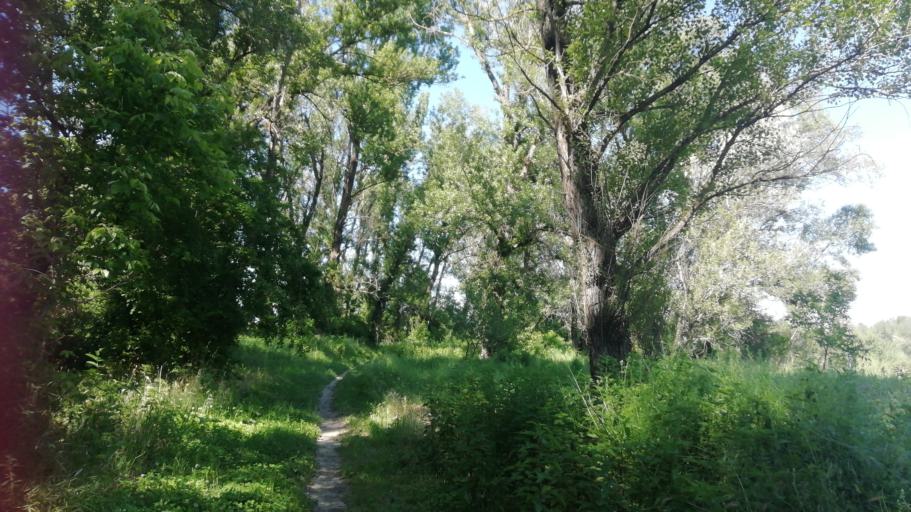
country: IT
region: Emilia-Romagna
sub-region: Provincia di Piacenza
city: Borgonovo Valtidone
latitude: 44.9794
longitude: 9.4598
